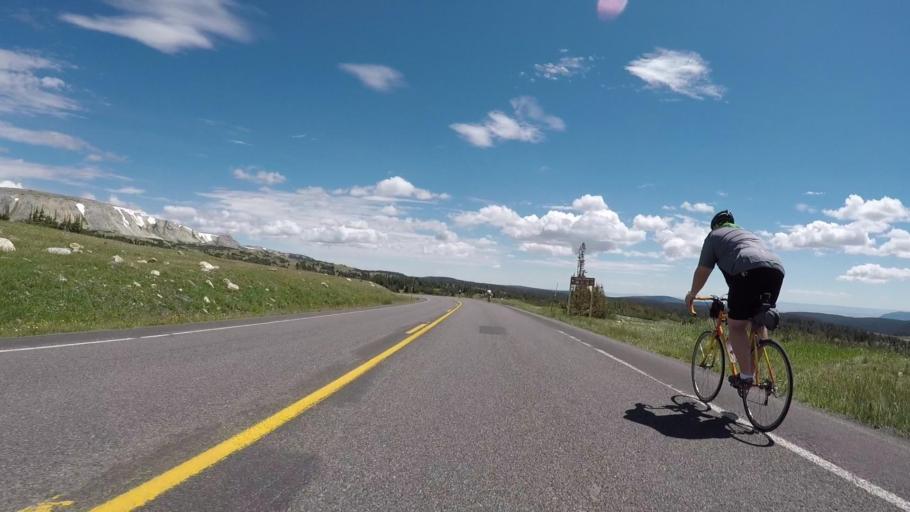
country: US
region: Wyoming
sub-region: Carbon County
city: Saratoga
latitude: 41.3449
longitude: -106.2919
